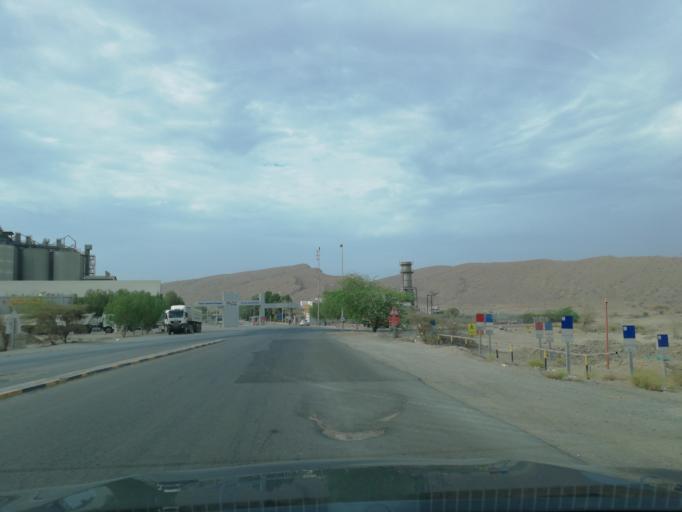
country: OM
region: Muhafazat Masqat
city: Bawshar
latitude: 23.4810
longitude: 58.2869
